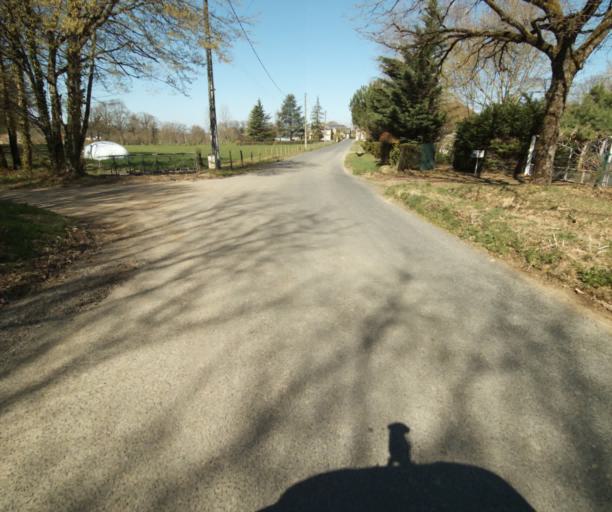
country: FR
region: Limousin
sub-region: Departement de la Correze
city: Saint-Clement
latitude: 45.3200
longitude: 1.6719
